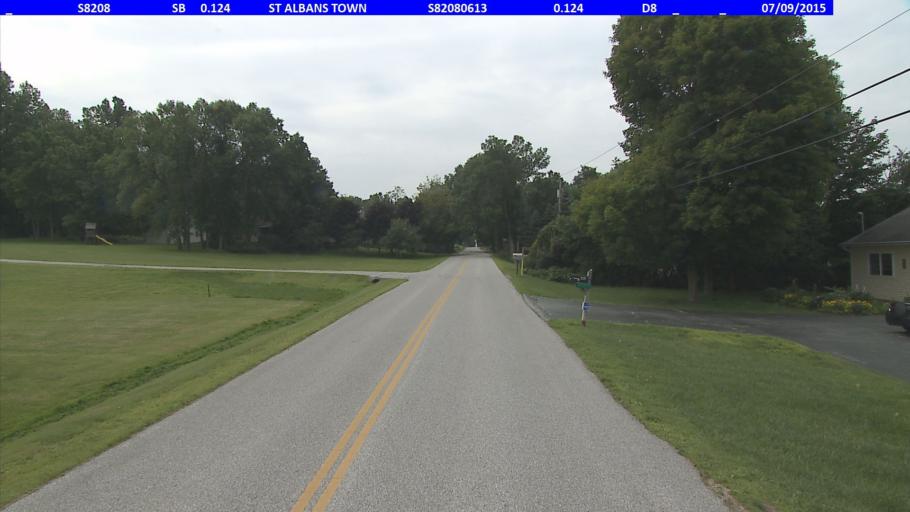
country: US
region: Vermont
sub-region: Franklin County
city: Saint Albans
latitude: 44.8258
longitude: -73.0758
